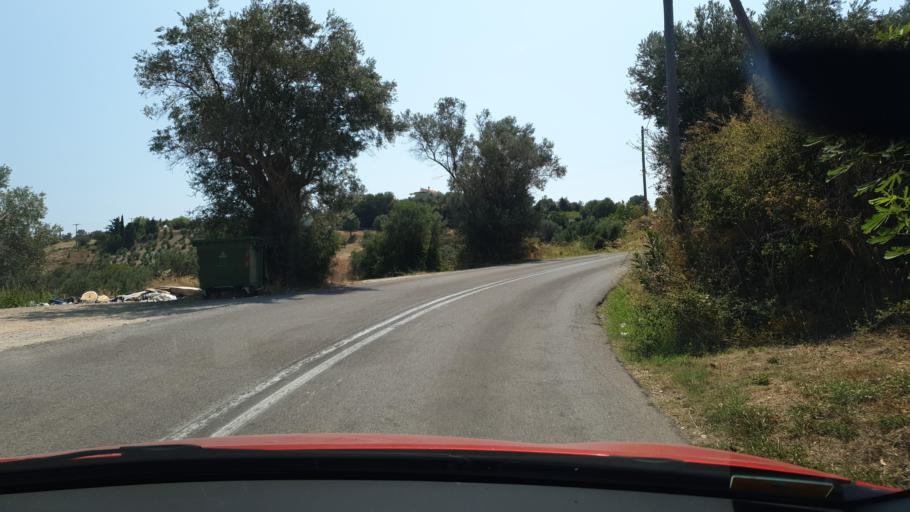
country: GR
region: Central Greece
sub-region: Nomos Evvoias
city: Oxilithos
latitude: 38.5350
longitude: 24.0822
